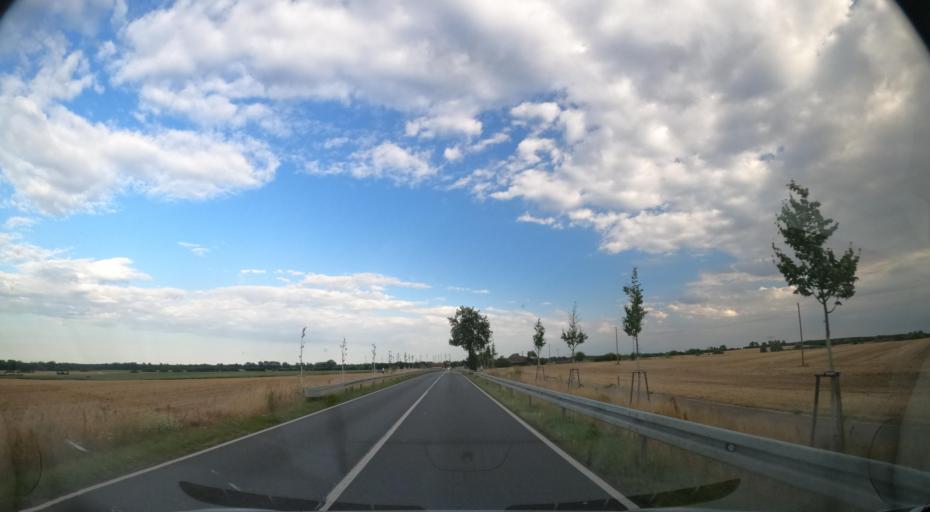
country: DE
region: Brandenburg
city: Brussow
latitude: 53.4829
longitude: 14.1087
